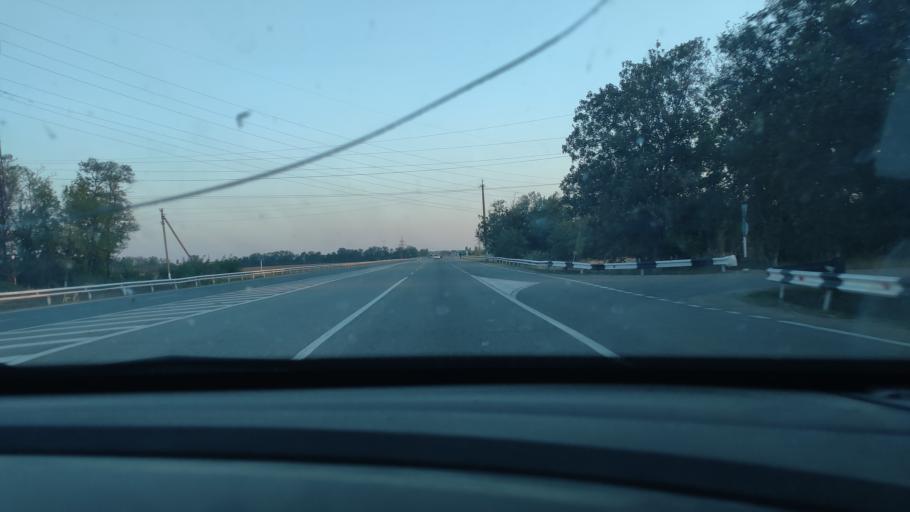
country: RU
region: Krasnodarskiy
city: Timashevsk
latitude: 45.6185
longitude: 38.9864
